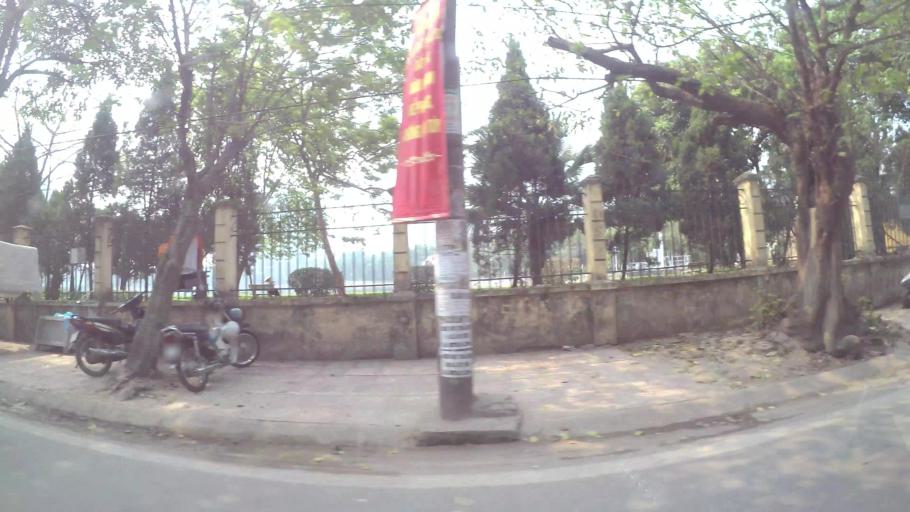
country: VN
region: Ha Noi
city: Cau Giay
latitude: 21.0204
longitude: 105.8127
